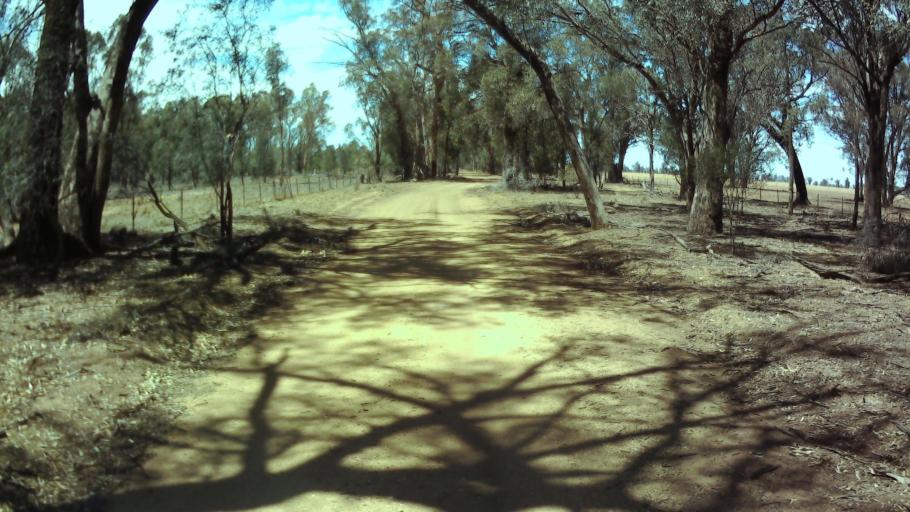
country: AU
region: New South Wales
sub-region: Weddin
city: Grenfell
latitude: -33.9126
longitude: 147.8063
